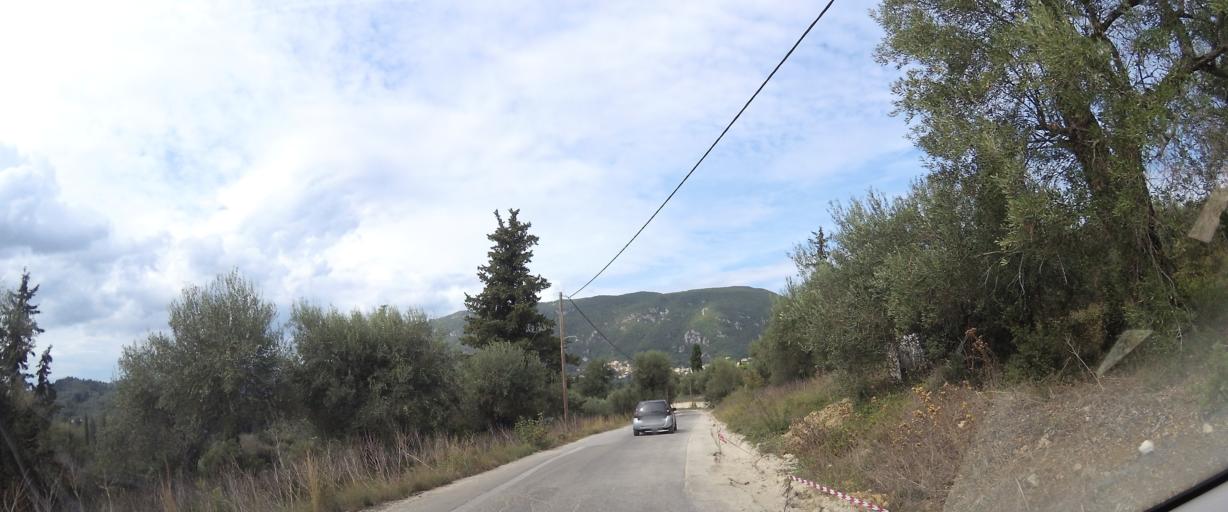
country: GR
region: Ionian Islands
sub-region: Nomos Kerkyras
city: Kontokali
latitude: 39.6948
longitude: 19.8077
